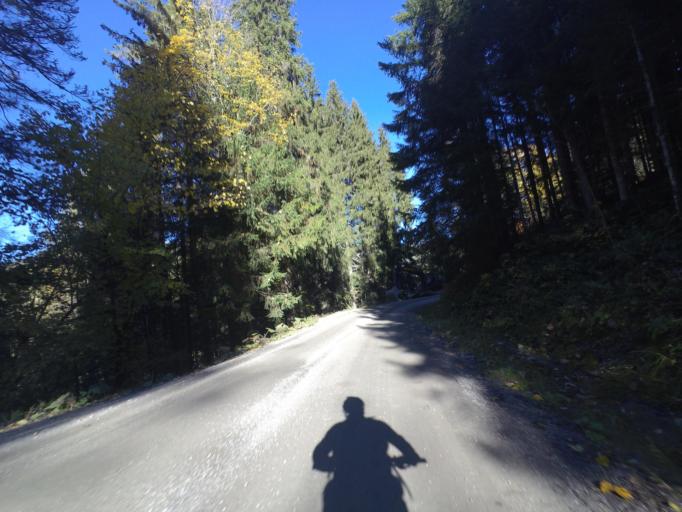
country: AT
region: Salzburg
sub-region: Politischer Bezirk Sankt Johann im Pongau
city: Sankt Johann im Pongau
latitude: 47.3263
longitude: 13.2326
